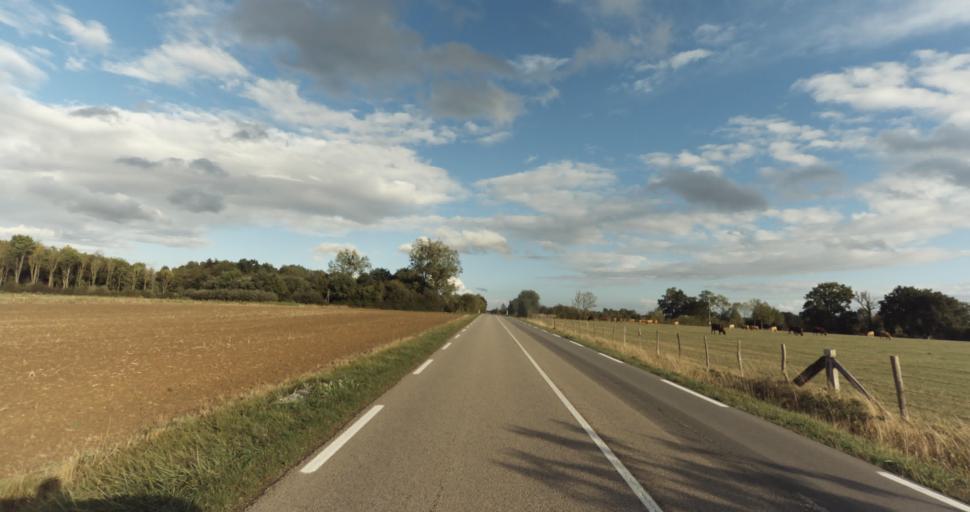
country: FR
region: Lower Normandy
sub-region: Departement de l'Orne
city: Sainte-Gauburge-Sainte-Colombe
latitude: 48.7287
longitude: 0.4076
